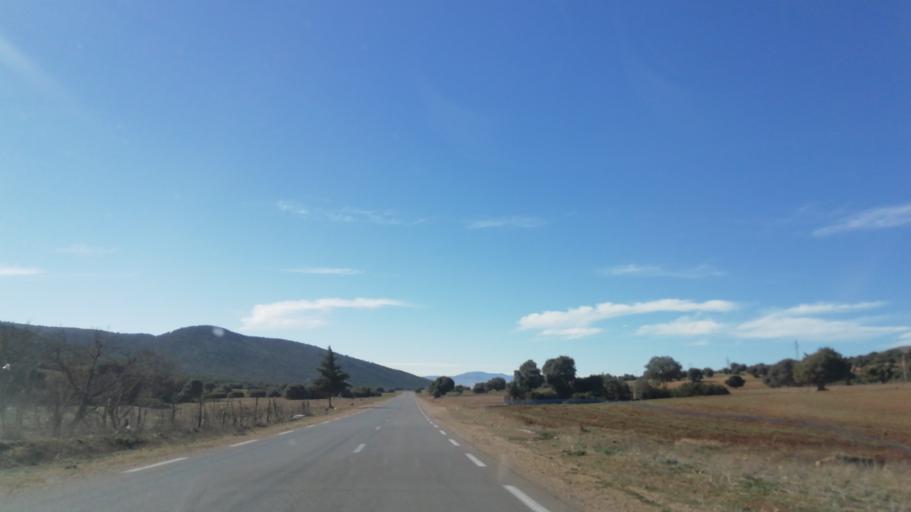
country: DZ
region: Tlemcen
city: Sebdou
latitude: 34.7101
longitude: -1.2121
